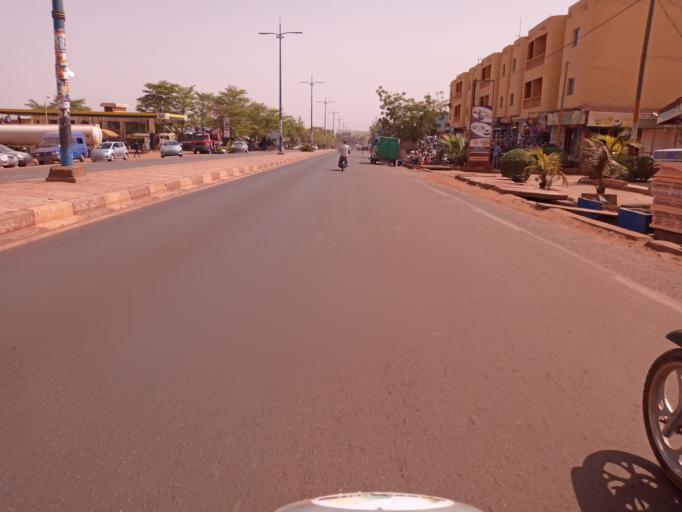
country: ML
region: Bamako
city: Bamako
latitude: 12.5871
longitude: -7.9918
